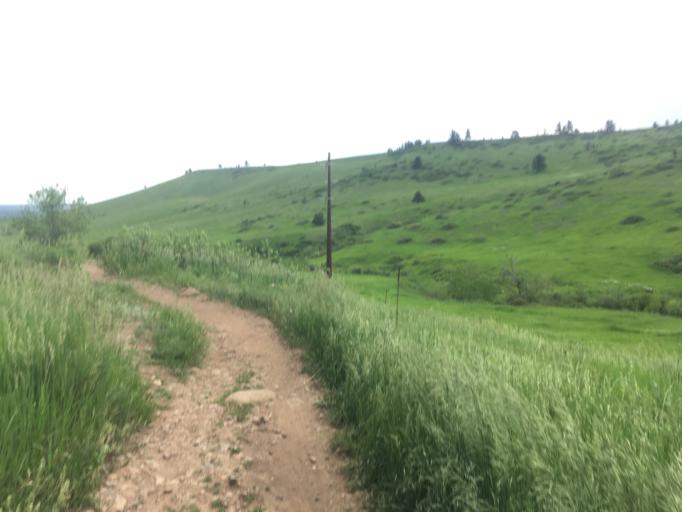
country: US
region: Colorado
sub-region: Boulder County
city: Boulder
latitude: 39.9256
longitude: -105.2580
